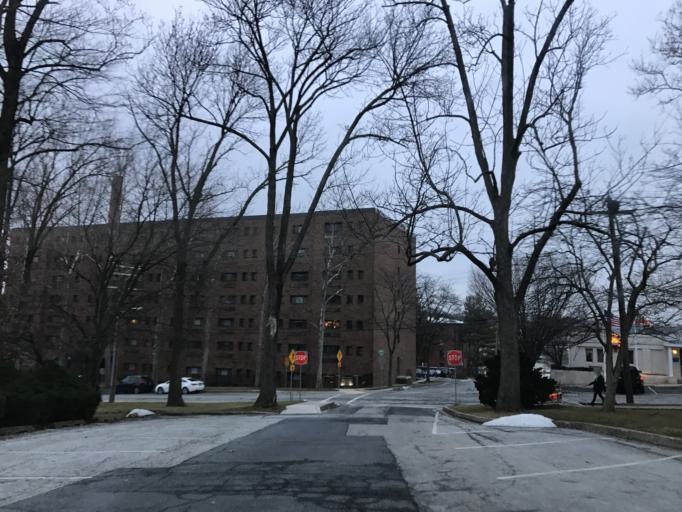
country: US
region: Maryland
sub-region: Carroll County
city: Westminster
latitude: 39.5753
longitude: -76.9926
